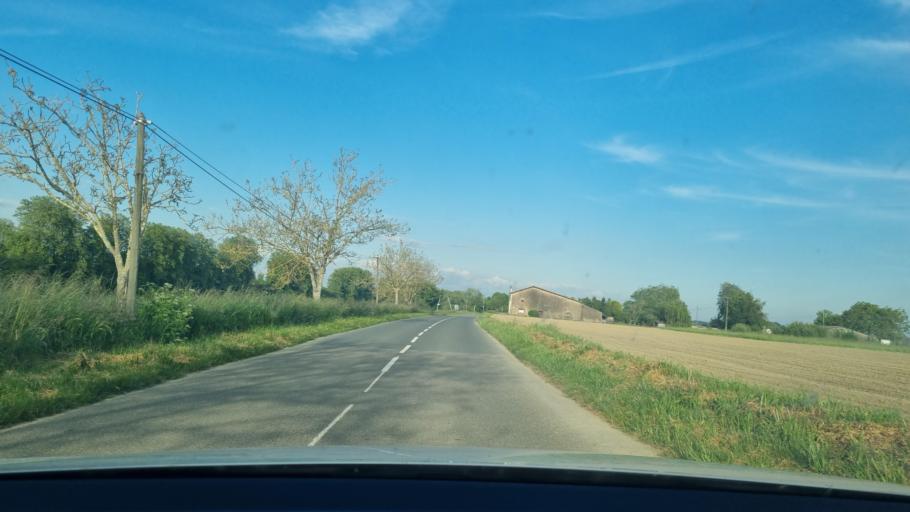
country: FR
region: Aquitaine
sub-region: Departement des Landes
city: Peyrehorade
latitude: 43.5467
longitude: -1.1880
